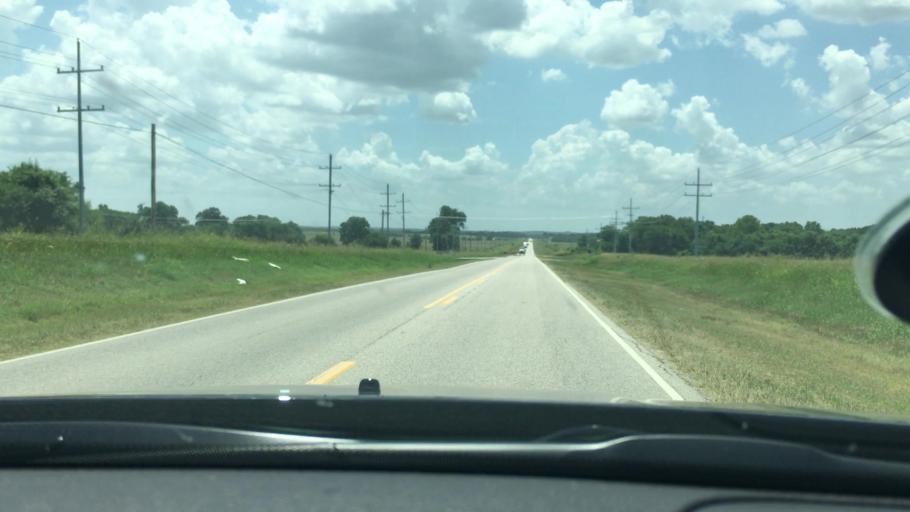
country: US
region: Oklahoma
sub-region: Pontotoc County
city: Ada
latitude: 34.6526
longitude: -96.6349
